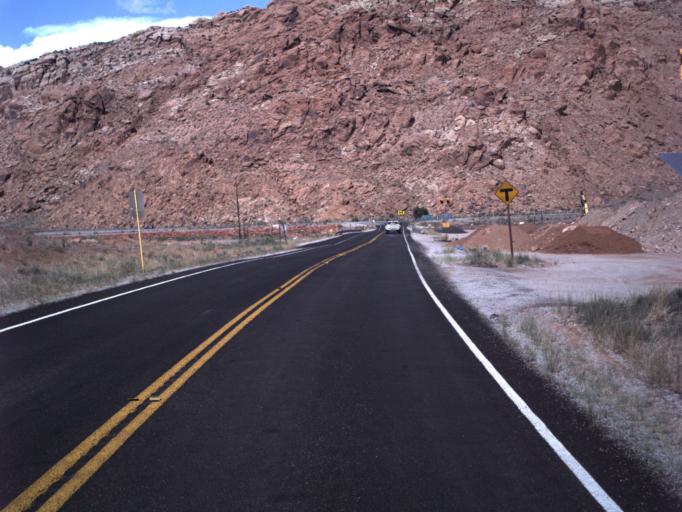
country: US
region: Utah
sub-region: Grand County
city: Moab
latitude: 38.6033
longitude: -109.6037
